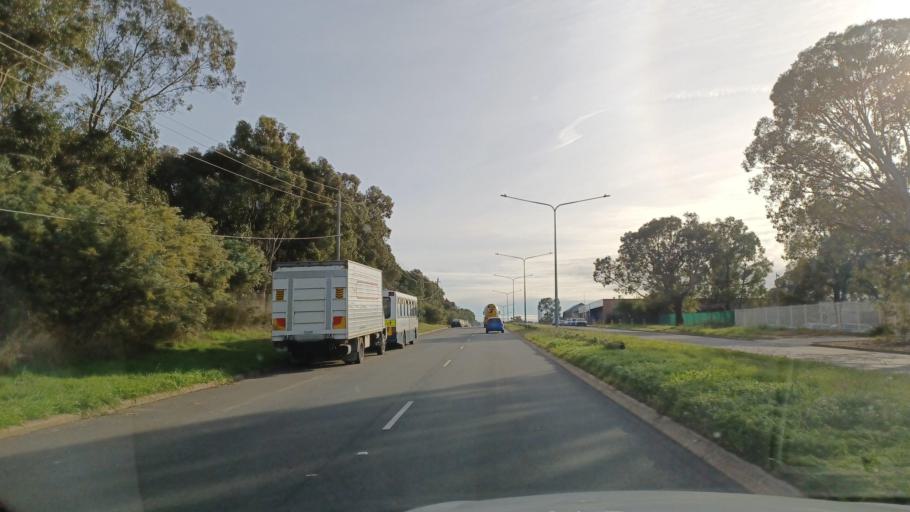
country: AU
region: Australian Capital Territory
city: Kaleen
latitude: -35.2190
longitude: 149.1367
